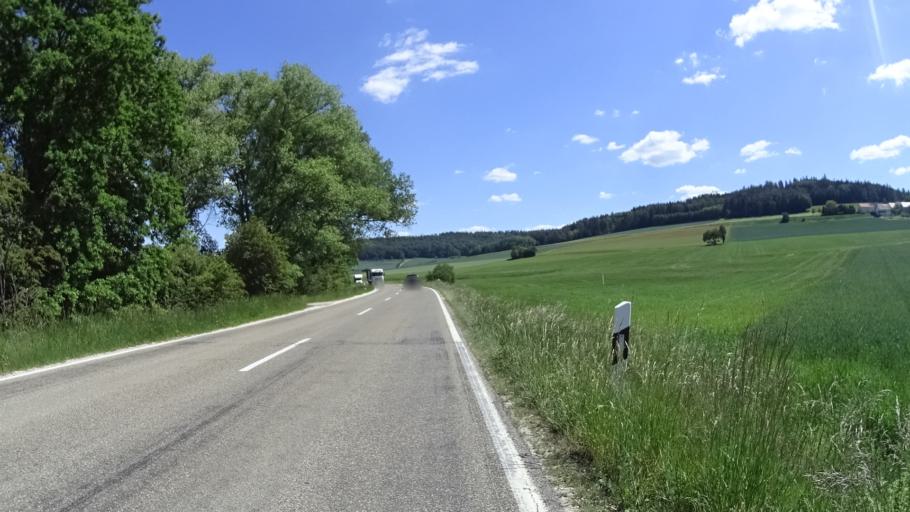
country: DE
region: Bavaria
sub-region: Regierungsbezirk Mittelfranken
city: Thalmassing
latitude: 49.0808
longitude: 11.2542
